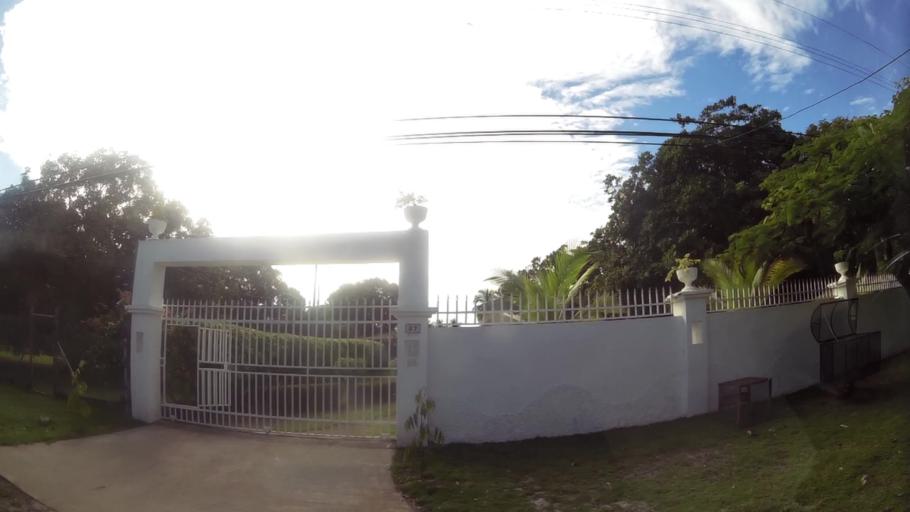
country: PA
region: Panama
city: Nueva Gorgona
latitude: 8.5308
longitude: -79.8815
